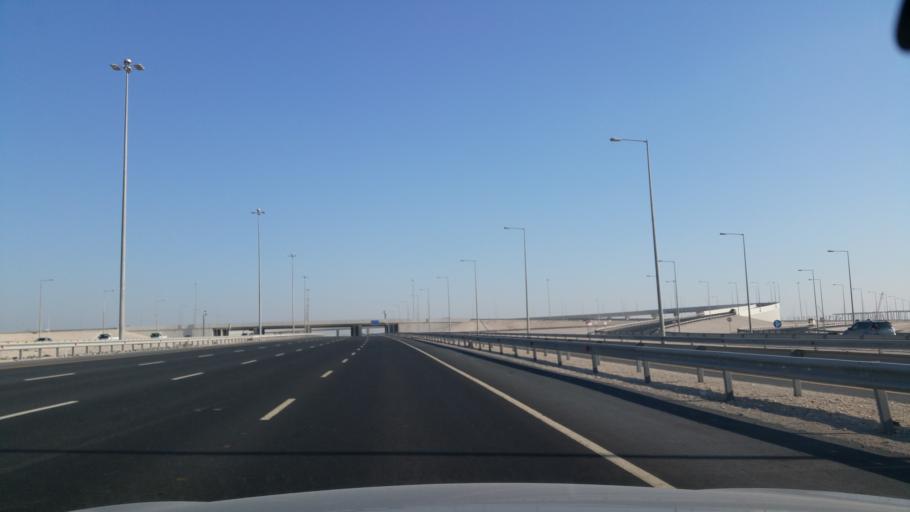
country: QA
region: Al Wakrah
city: Al Wukayr
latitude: 25.1263
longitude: 51.4837
